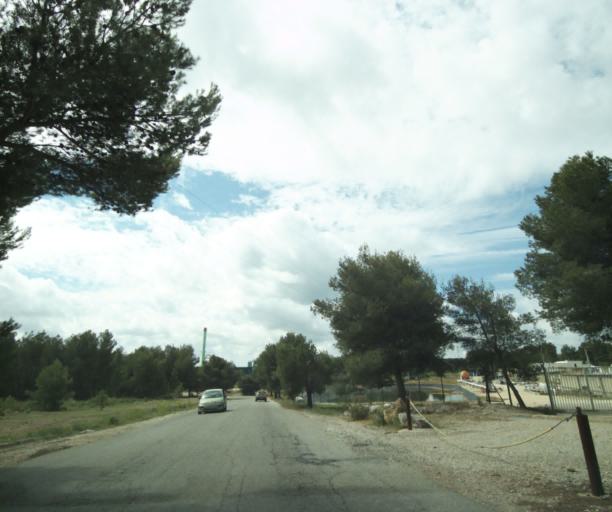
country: FR
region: Provence-Alpes-Cote d'Azur
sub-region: Departement des Bouches-du-Rhone
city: Rognac
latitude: 43.5009
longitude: 5.2083
